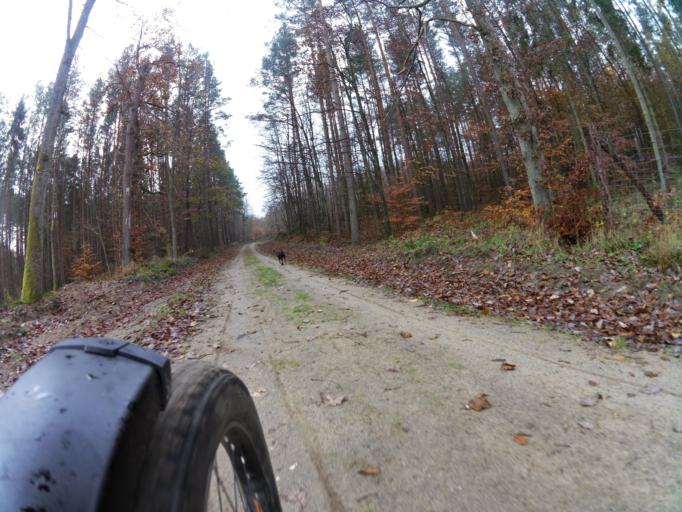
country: PL
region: Pomeranian Voivodeship
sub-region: Powiat pucki
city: Krokowa
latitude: 54.7781
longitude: 18.0920
